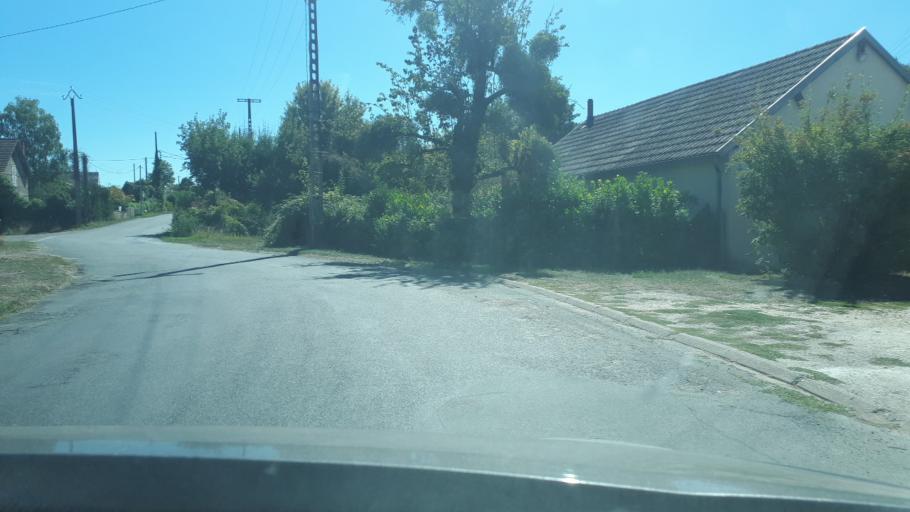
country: FR
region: Centre
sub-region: Departement du Cher
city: Sancerre
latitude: 47.2524
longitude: 2.7604
